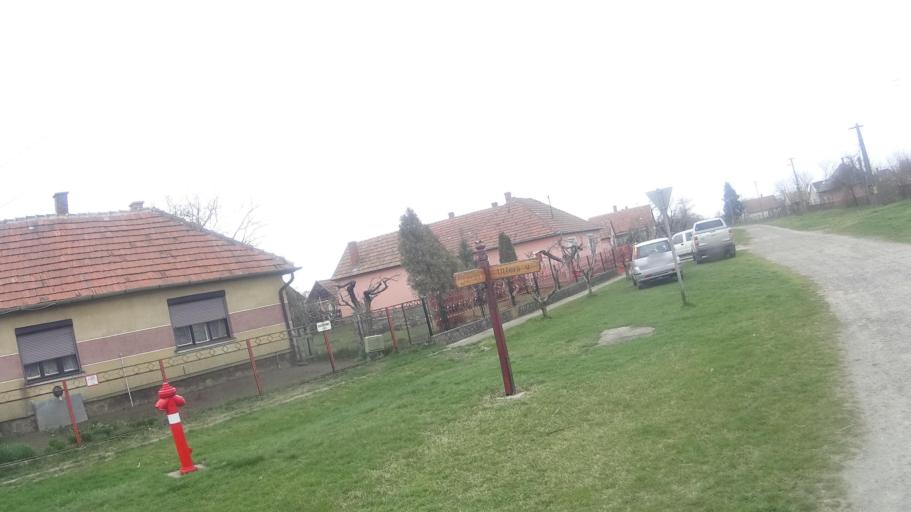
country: HU
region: Fejer
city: Sarosd
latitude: 46.9794
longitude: 18.6325
